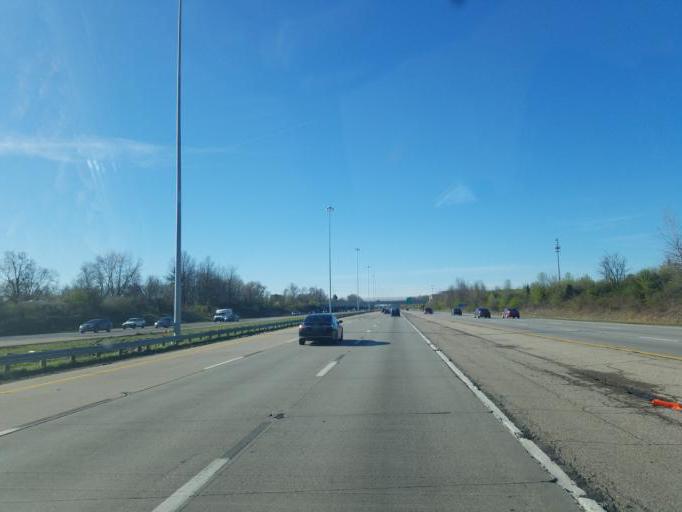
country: US
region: Ohio
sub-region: Franklin County
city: Gahanna
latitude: 40.0380
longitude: -82.9033
